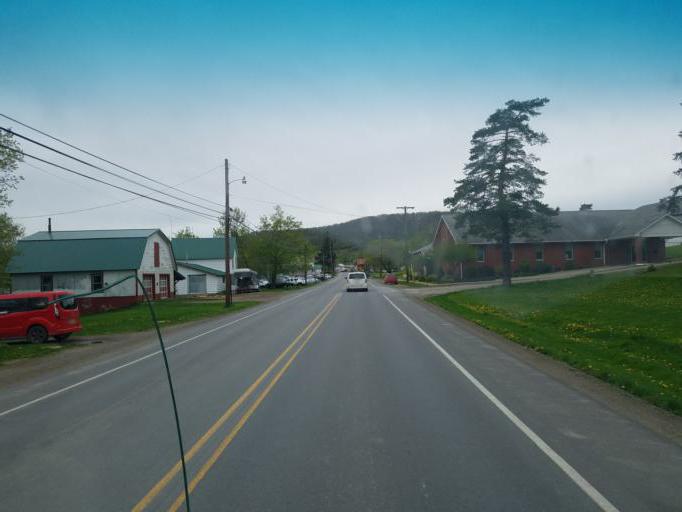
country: US
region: Pennsylvania
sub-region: Tioga County
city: Westfield
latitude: 41.9390
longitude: -77.6456
